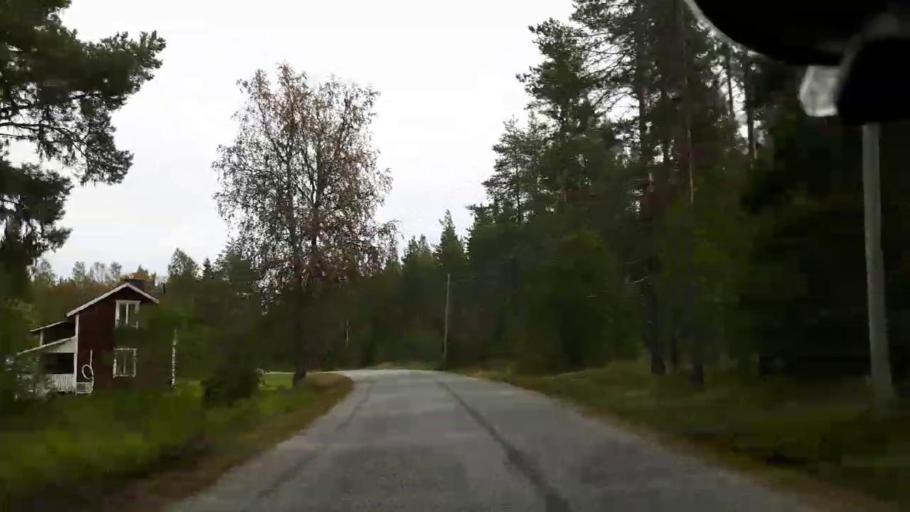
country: SE
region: Jaemtland
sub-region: Ragunda Kommun
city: Hammarstrand
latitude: 63.0109
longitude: 16.1109
